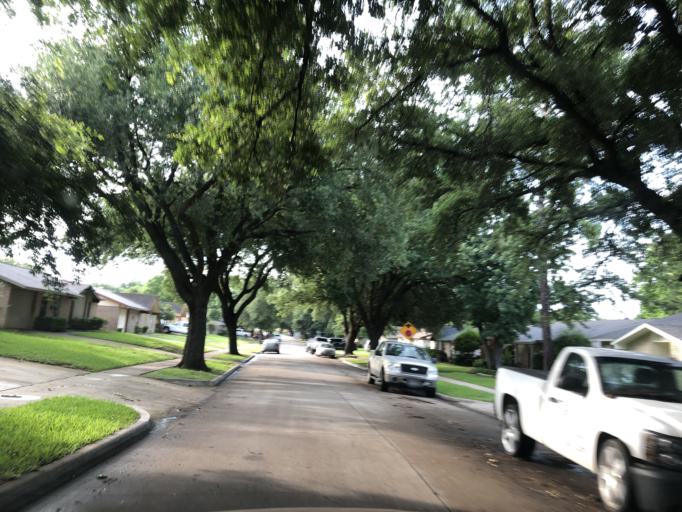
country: US
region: Texas
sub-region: Dallas County
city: Sunnyvale
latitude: 32.8484
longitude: -96.6021
